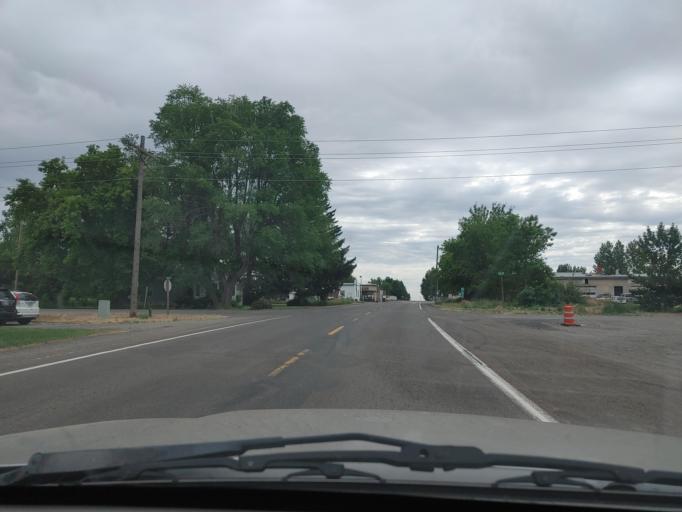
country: US
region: Idaho
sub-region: Lincoln County
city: Shoshone
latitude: 43.0493
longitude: -114.1558
